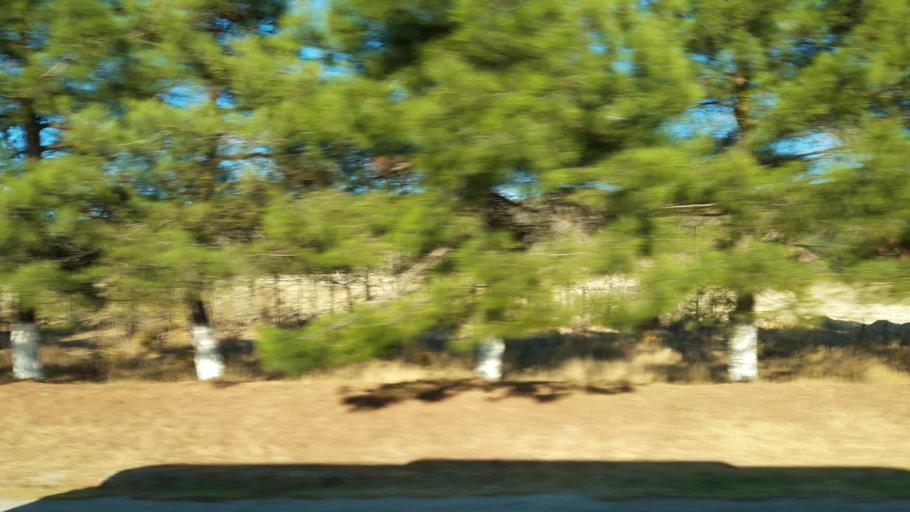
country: RU
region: Krasnodarskiy
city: Kabardinka
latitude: 44.6303
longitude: 38.0029
